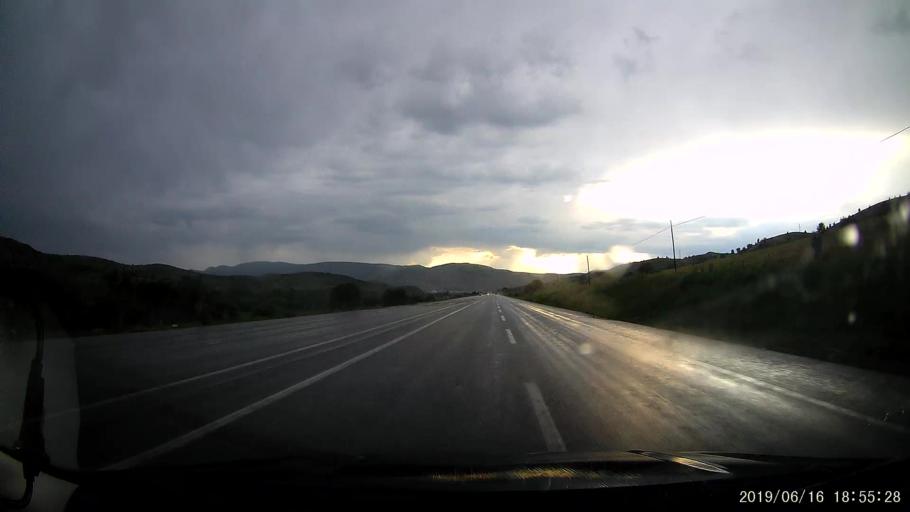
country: TR
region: Erzincan
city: Refahiye
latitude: 39.9002
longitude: 38.8271
